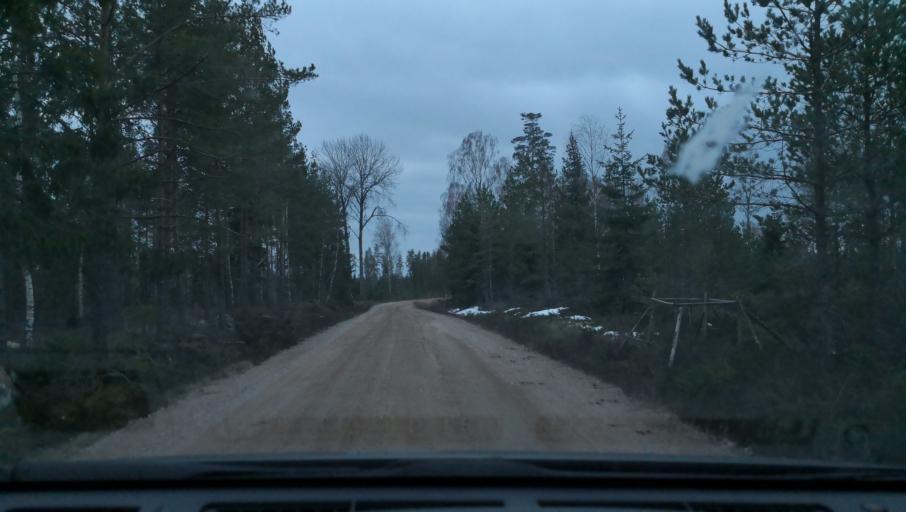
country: SE
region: OErebro
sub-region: Lindesbergs Kommun
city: Fellingsbro
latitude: 59.5901
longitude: 15.5768
